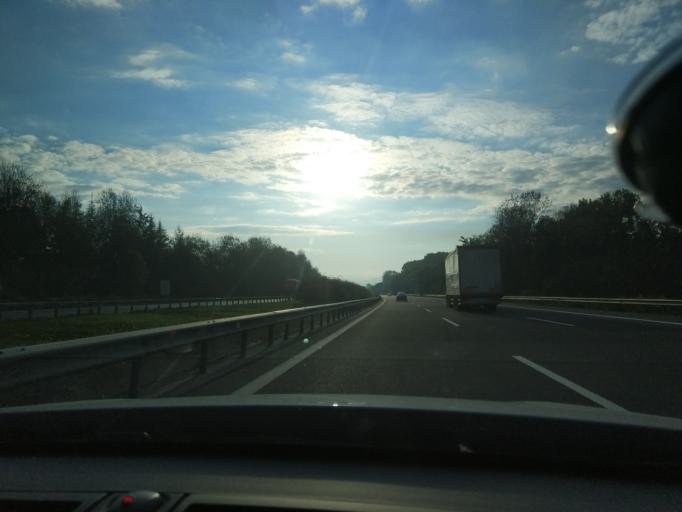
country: TR
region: Duzce
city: Duzce
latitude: 40.8072
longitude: 31.1492
